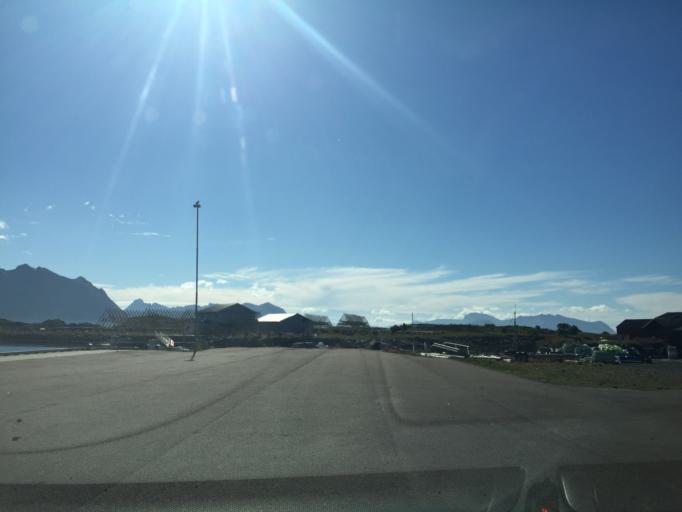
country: NO
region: Nordland
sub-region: Vagan
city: Kabelvag
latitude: 68.3868
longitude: 14.4149
